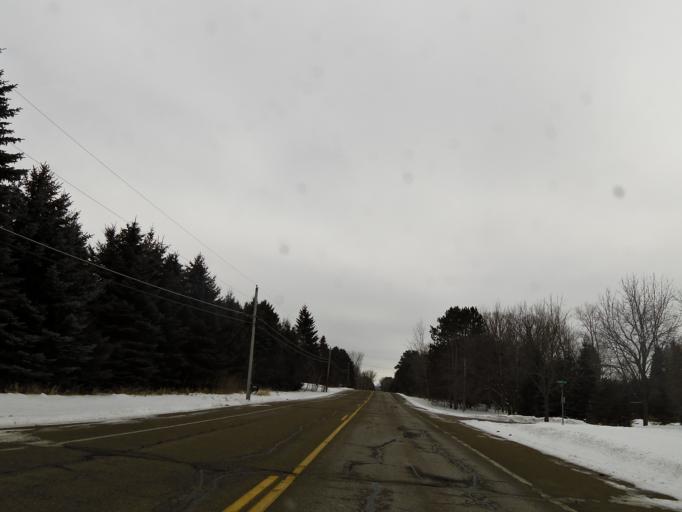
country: US
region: Minnesota
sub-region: Washington County
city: Lakeland
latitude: 44.9753
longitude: -92.8224
